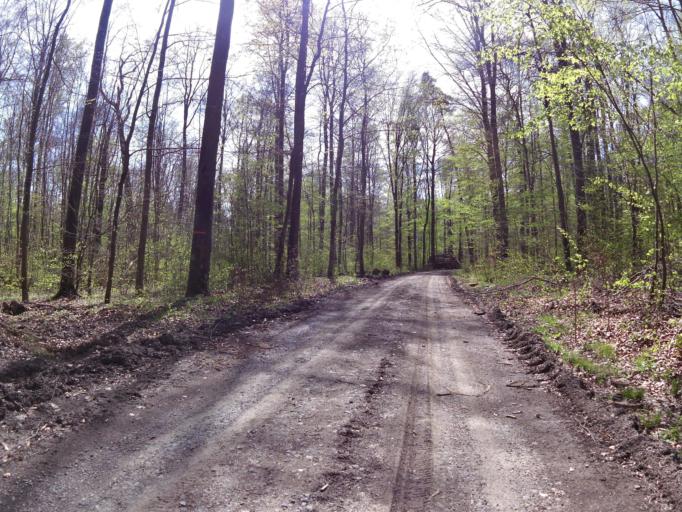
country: DE
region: Bavaria
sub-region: Regierungsbezirk Unterfranken
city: Rimpar
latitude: 49.8627
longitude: 9.9850
